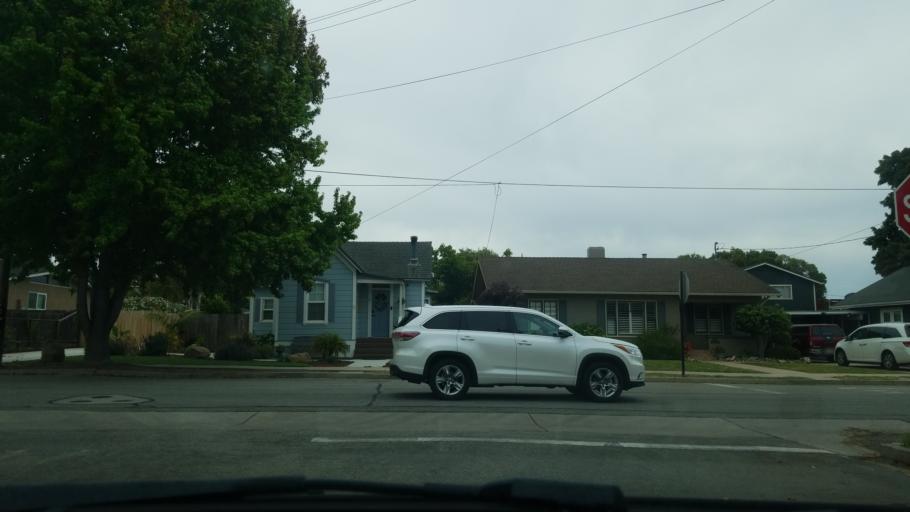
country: US
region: California
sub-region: San Luis Obispo County
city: Arroyo Grande
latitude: 35.1208
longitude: -120.5738
